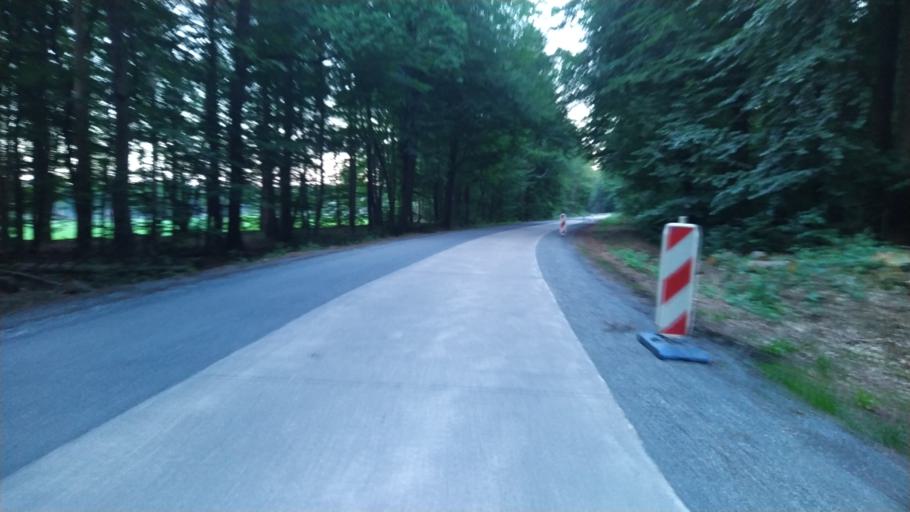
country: DE
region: Lower Saxony
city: Deinstedt
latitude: 53.4917
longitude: 9.2237
